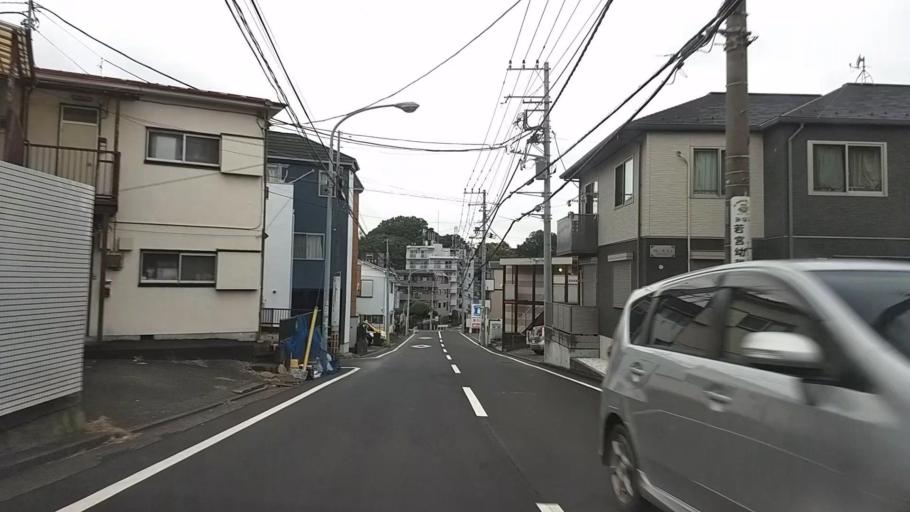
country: JP
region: Kanagawa
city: Yokohama
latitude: 35.4133
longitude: 139.6049
